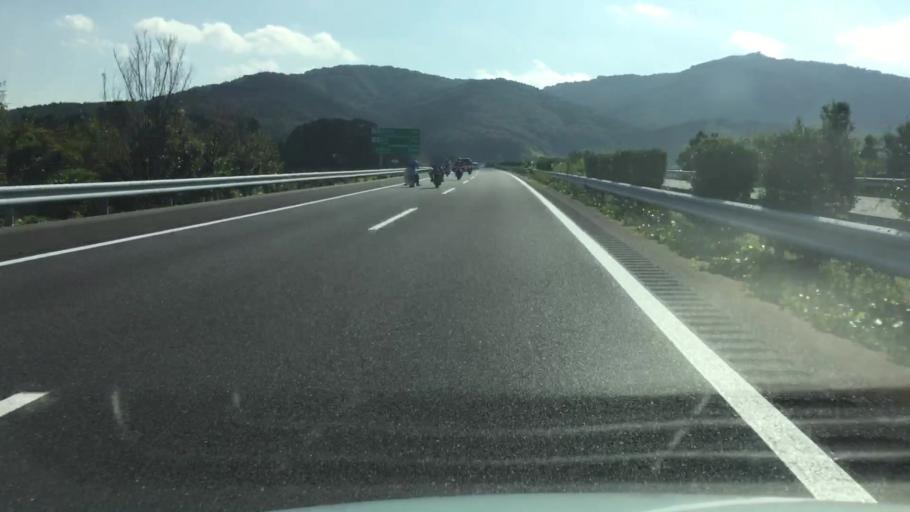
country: JP
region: Ibaraki
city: Iwase
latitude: 36.3537
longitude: 140.0959
